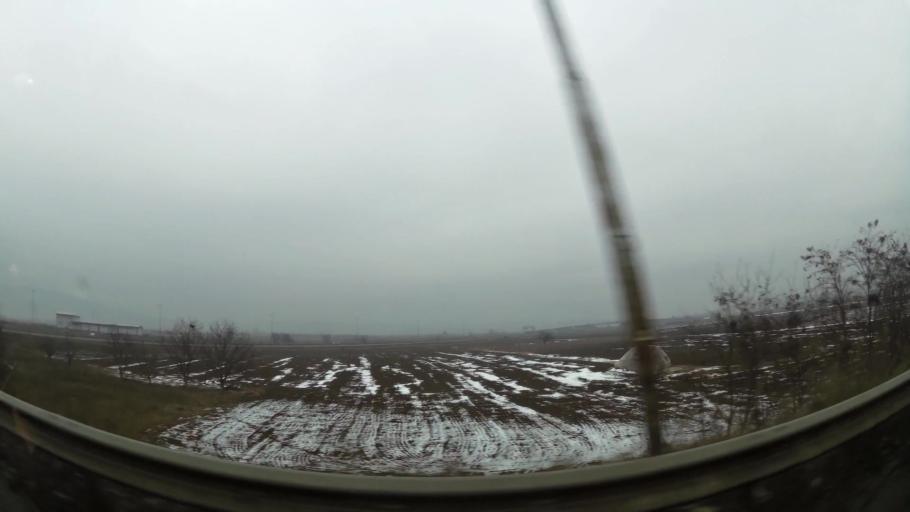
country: MK
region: Suto Orizari
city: Suto Orizare
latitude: 42.0517
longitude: 21.3832
